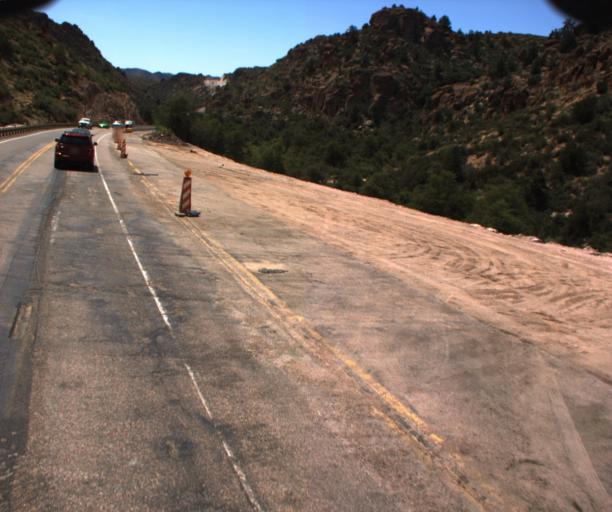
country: US
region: Arizona
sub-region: Pinal County
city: Superior
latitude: 33.3291
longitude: -111.0314
